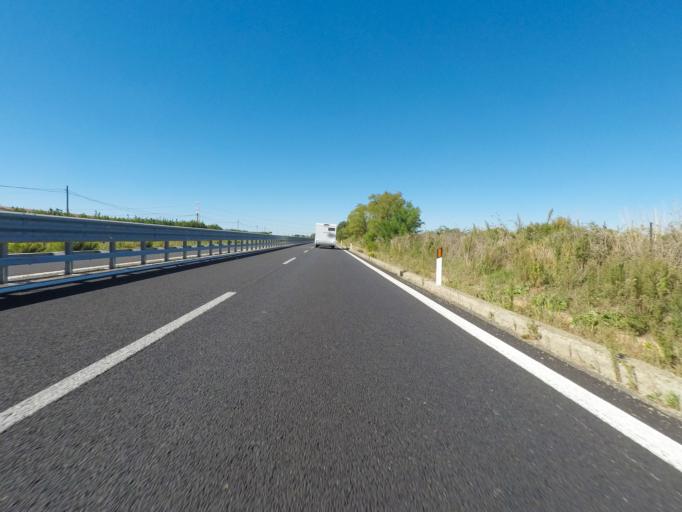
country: IT
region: Latium
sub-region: Provincia di Viterbo
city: Tarquinia
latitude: 42.2750
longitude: 11.7067
